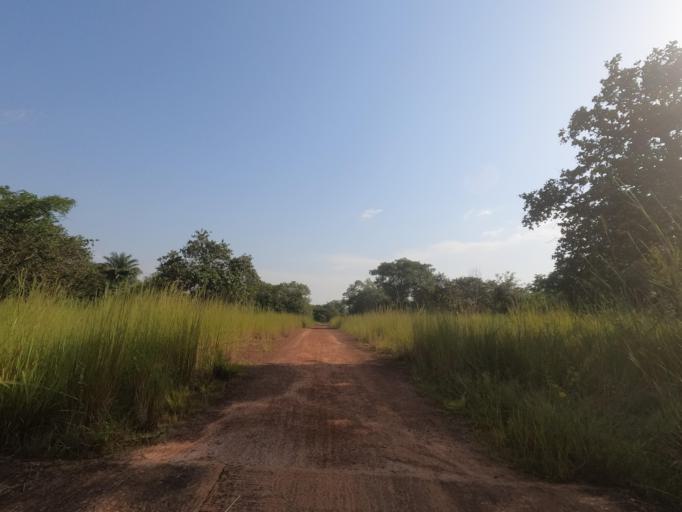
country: SN
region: Sedhiou
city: Sedhiou
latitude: 12.4343
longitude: -15.7377
